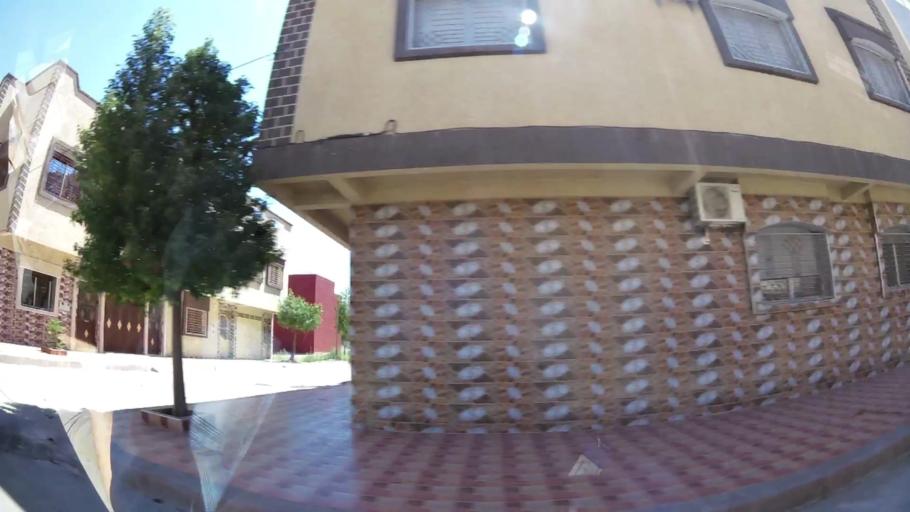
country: MA
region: Oriental
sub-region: Oujda-Angad
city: Oujda
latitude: 34.6855
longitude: -1.9469
